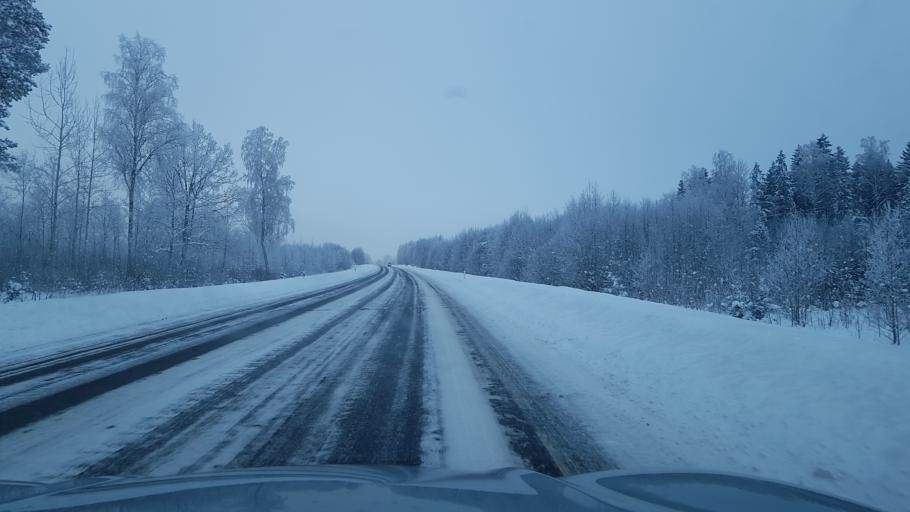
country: EE
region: Ida-Virumaa
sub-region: Johvi vald
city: Johvi
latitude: 59.2196
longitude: 27.3377
